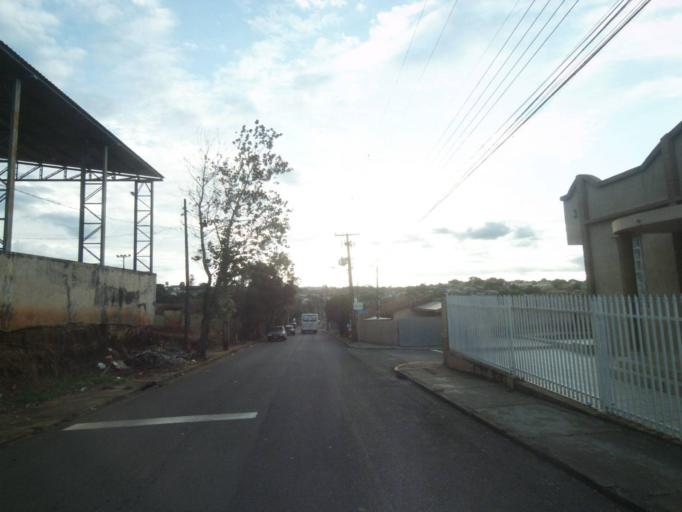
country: BR
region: Parana
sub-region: Telemaco Borba
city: Telemaco Borba
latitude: -24.3242
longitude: -50.6419
